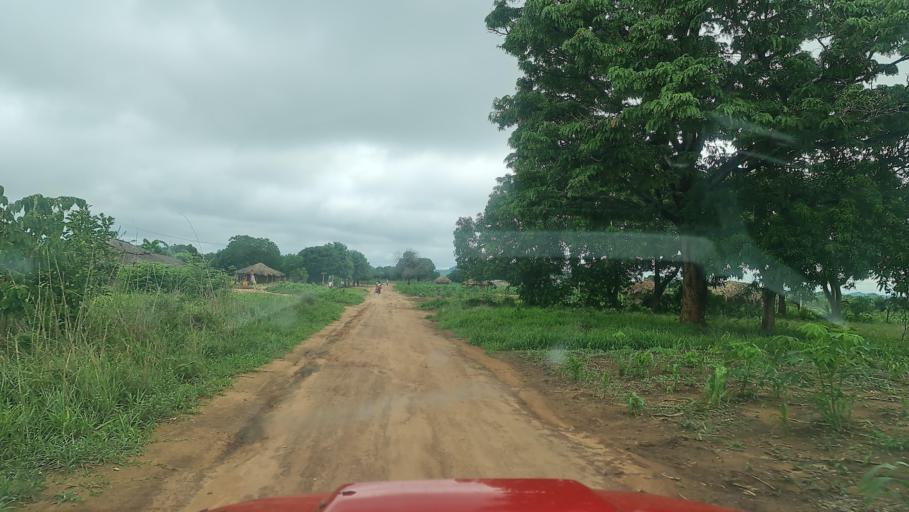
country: MW
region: Southern Region
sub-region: Nsanje District
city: Nsanje
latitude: -17.1955
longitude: 35.8455
